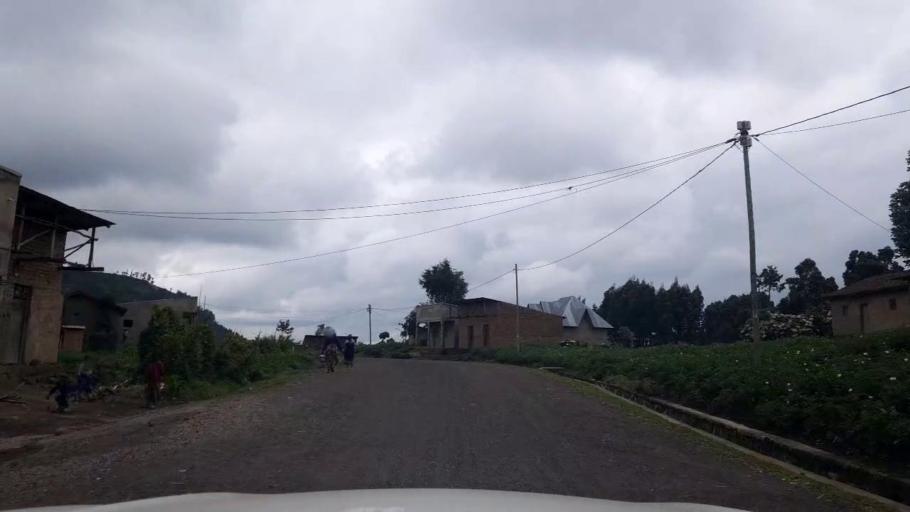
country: RW
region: Northern Province
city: Musanze
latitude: -1.5845
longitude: 29.4733
